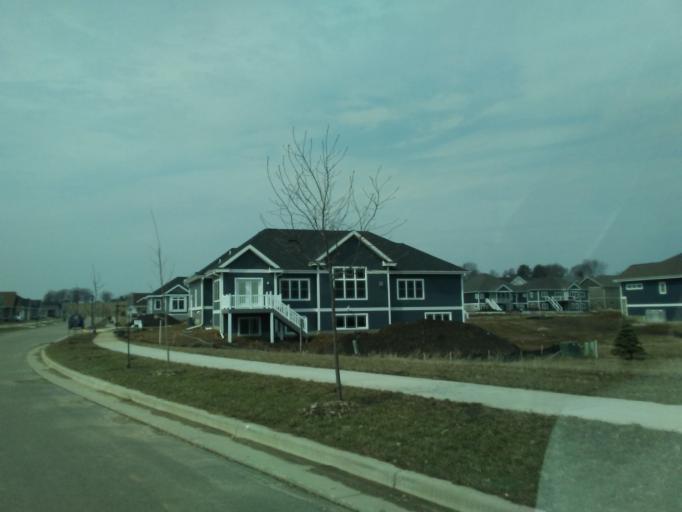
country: US
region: Wisconsin
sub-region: Dane County
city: Waunakee
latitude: 43.1744
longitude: -89.4517
